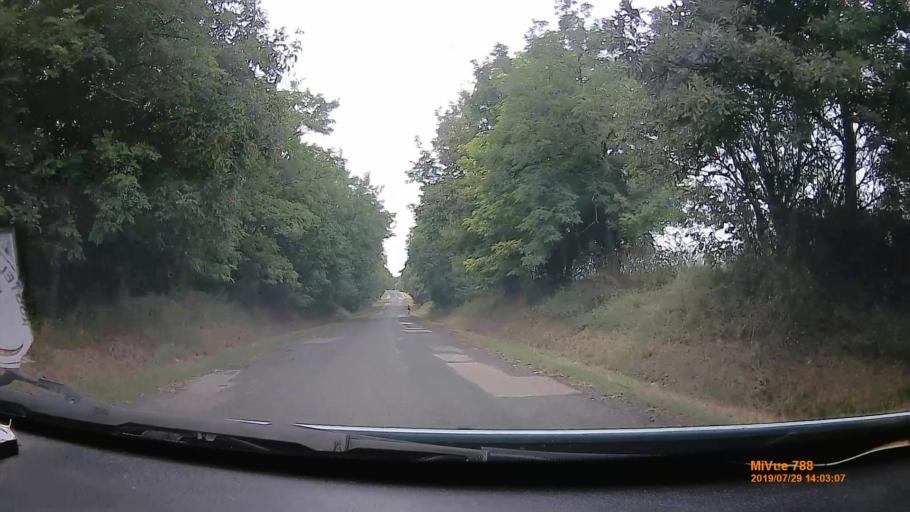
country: HU
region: Somogy
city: Balatonfoldvar
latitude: 46.8098
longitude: 17.9270
